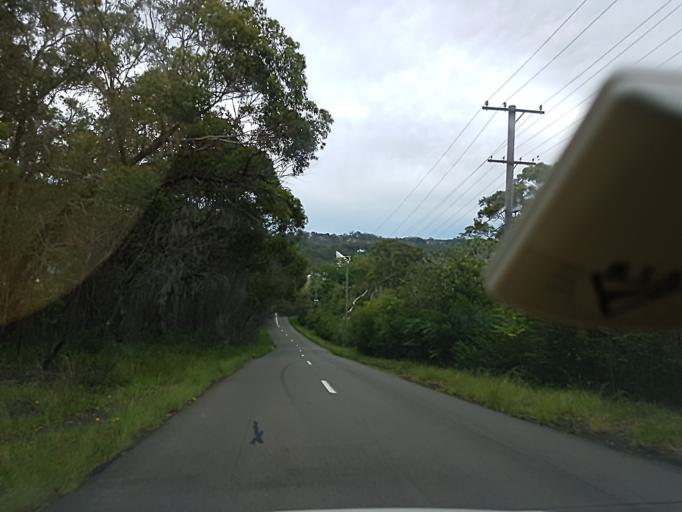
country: AU
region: New South Wales
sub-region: Warringah
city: Allambie Heights
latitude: -33.7308
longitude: 151.2372
